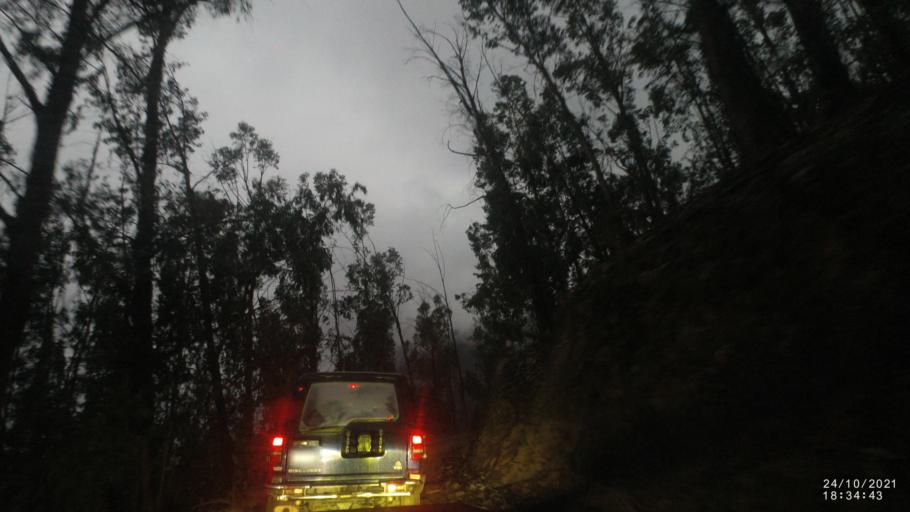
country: BO
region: Cochabamba
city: Cochabamba
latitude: -17.3399
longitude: -66.1446
